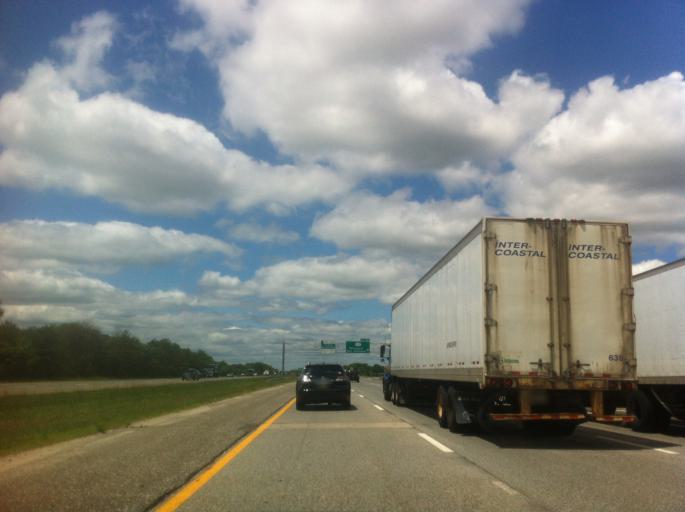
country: US
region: New York
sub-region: Suffolk County
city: Medford
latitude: 40.8232
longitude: -72.9877
